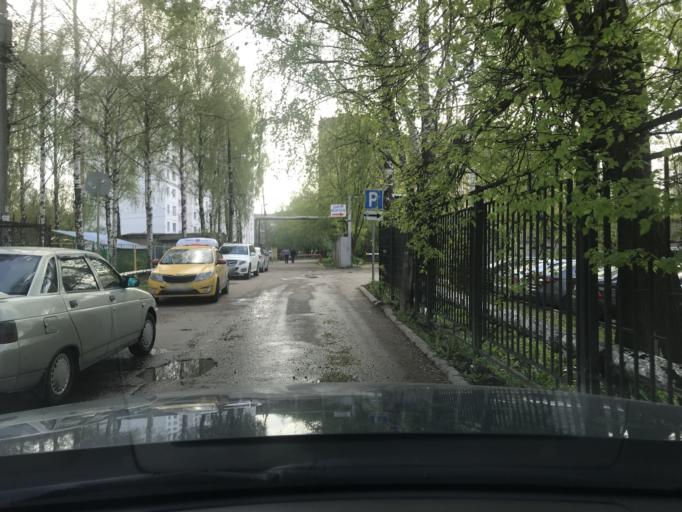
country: RU
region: Moskovskaya
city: Naro-Fominsk
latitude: 55.3882
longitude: 36.7436
